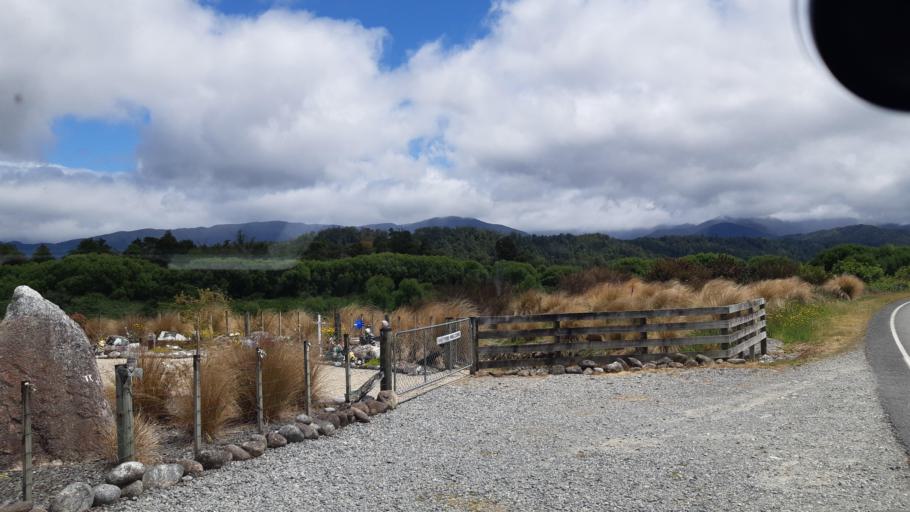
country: NZ
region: West Coast
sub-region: Grey District
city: Greymouth
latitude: -42.3160
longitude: 171.5407
